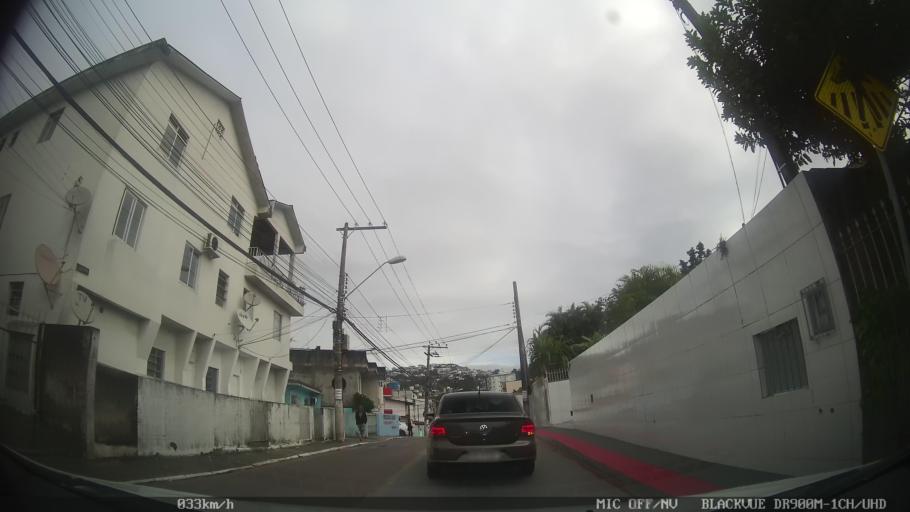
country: BR
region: Santa Catarina
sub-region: Sao Jose
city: Campinas
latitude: -27.5778
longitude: -48.6210
